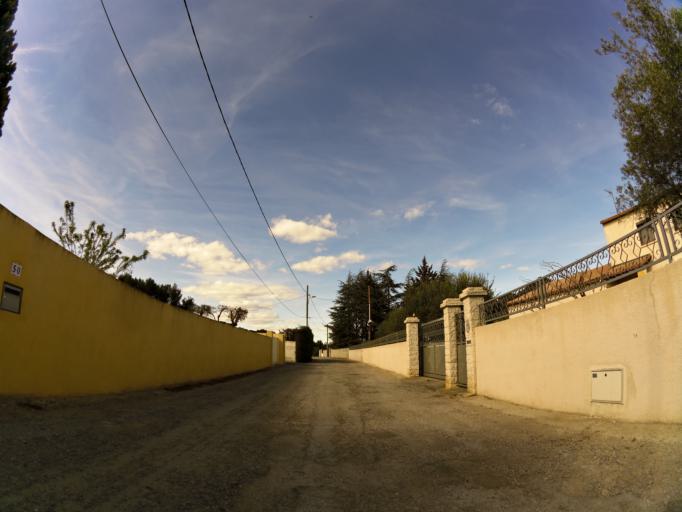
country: FR
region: Languedoc-Roussillon
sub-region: Departement du Gard
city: Mus
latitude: 43.7438
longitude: 4.2009
